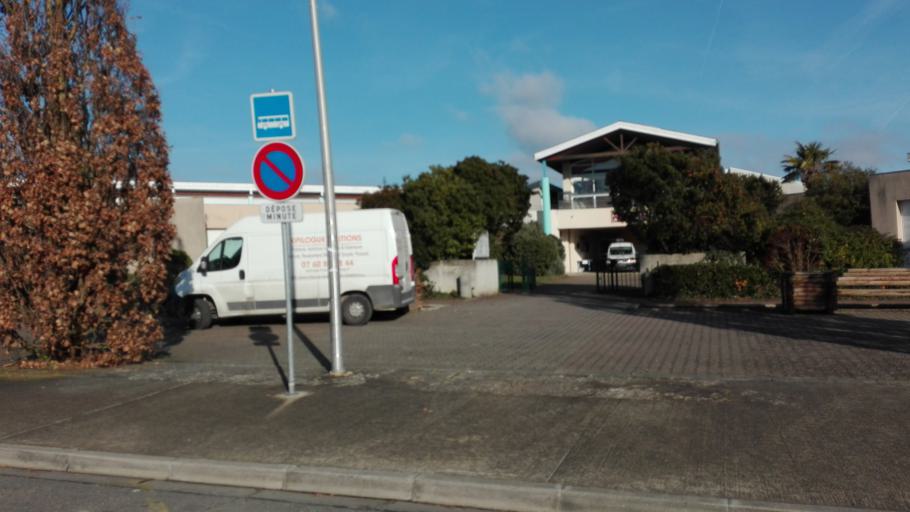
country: FR
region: Midi-Pyrenees
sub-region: Departement de la Haute-Garonne
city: Grenade
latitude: 43.7671
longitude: 1.2982
